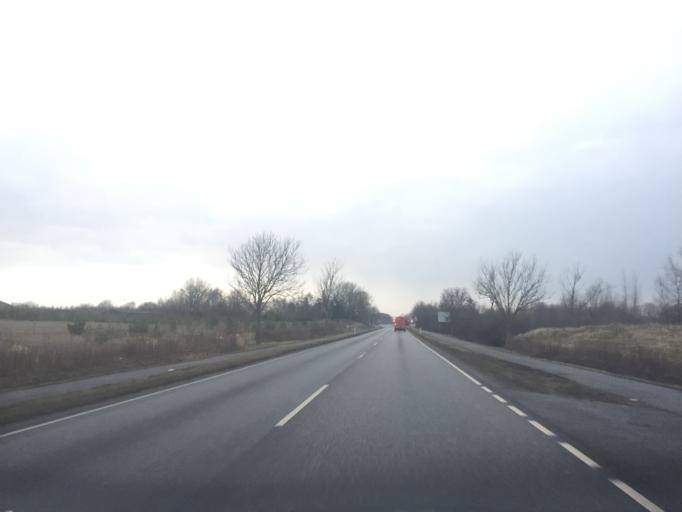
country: DK
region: Zealand
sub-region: Greve Kommune
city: Greve
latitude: 55.5860
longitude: 12.2433
